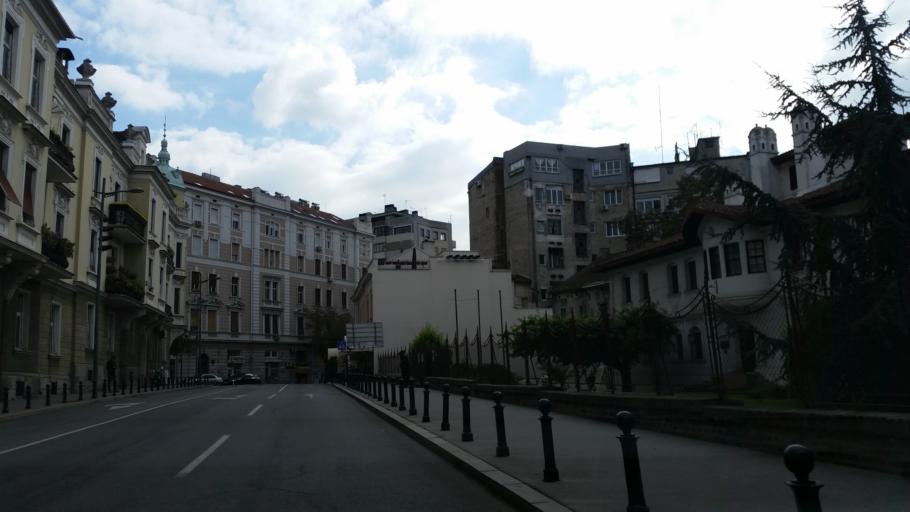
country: RS
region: Central Serbia
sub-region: Belgrade
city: Stari Grad
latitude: 44.8175
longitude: 20.4523
